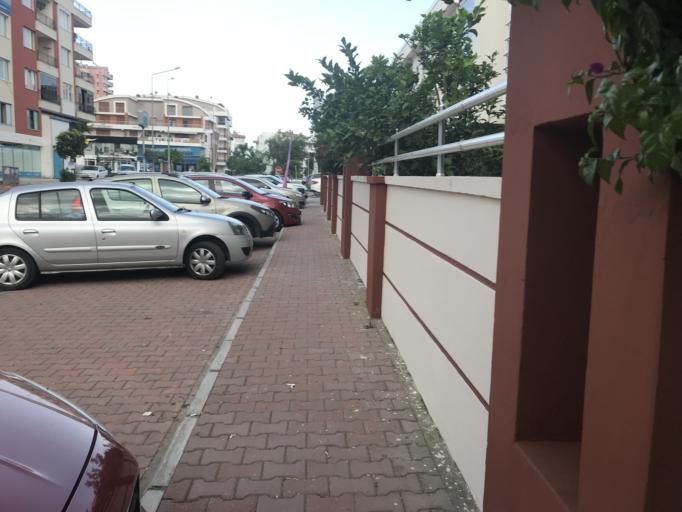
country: TR
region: Antalya
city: Cakirlar
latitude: 36.8492
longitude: 30.6123
